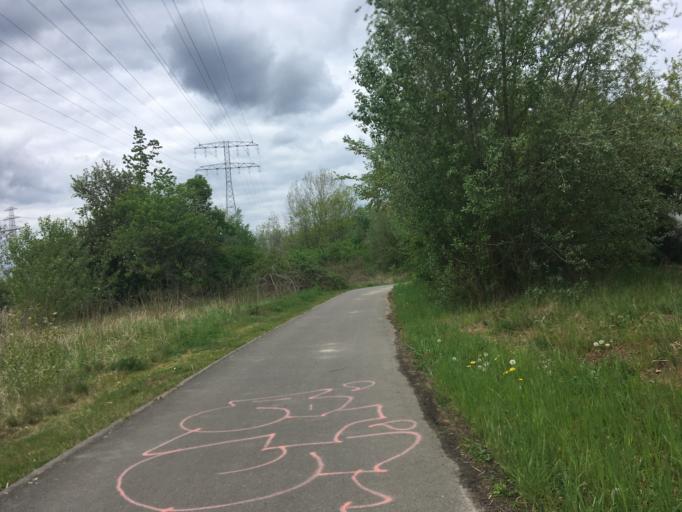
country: DE
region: Berlin
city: Falkenberg
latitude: 52.5445
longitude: 13.5319
